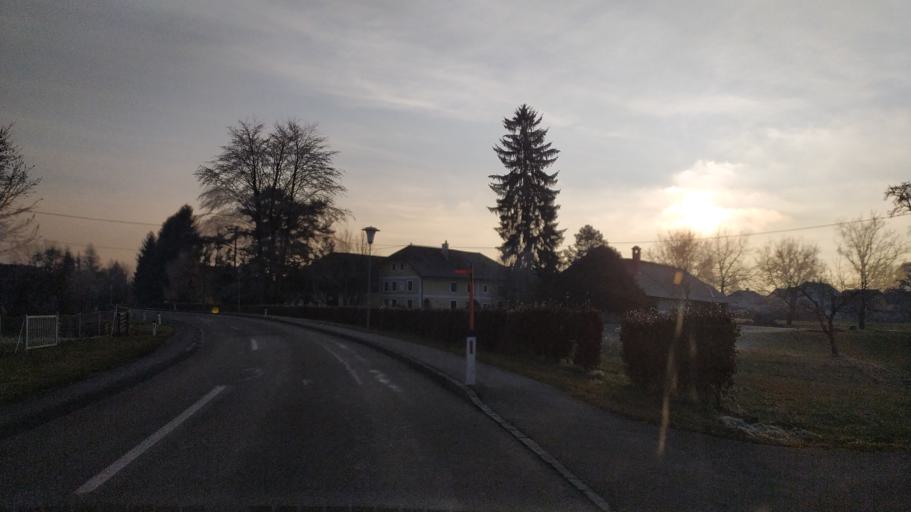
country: AT
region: Upper Austria
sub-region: Politischer Bezirk Urfahr-Umgebung
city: Goldworth
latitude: 48.3328
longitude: 14.0972
